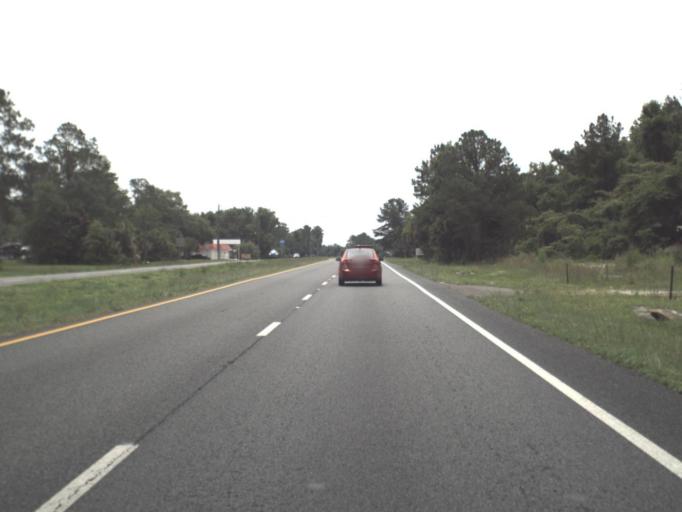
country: US
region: Florida
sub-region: Nassau County
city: Hilliard
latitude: 30.6504
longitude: -81.8740
